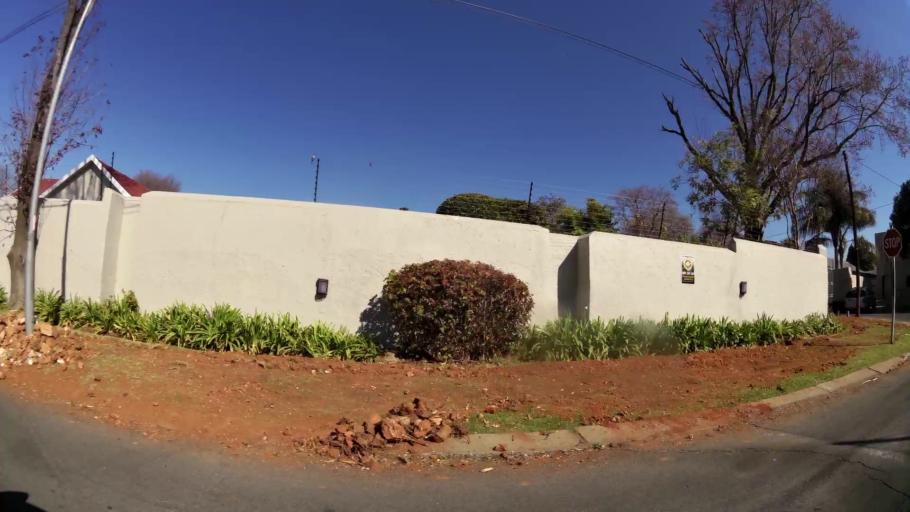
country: ZA
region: Gauteng
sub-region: City of Johannesburg Metropolitan Municipality
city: Modderfontein
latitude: -26.1392
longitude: 28.1109
